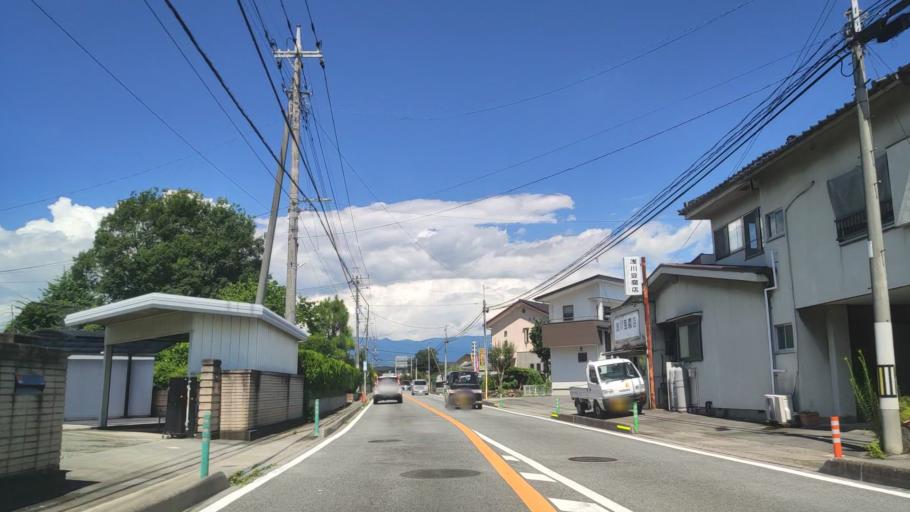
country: JP
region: Yamanashi
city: Isawa
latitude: 35.6661
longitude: 138.6453
